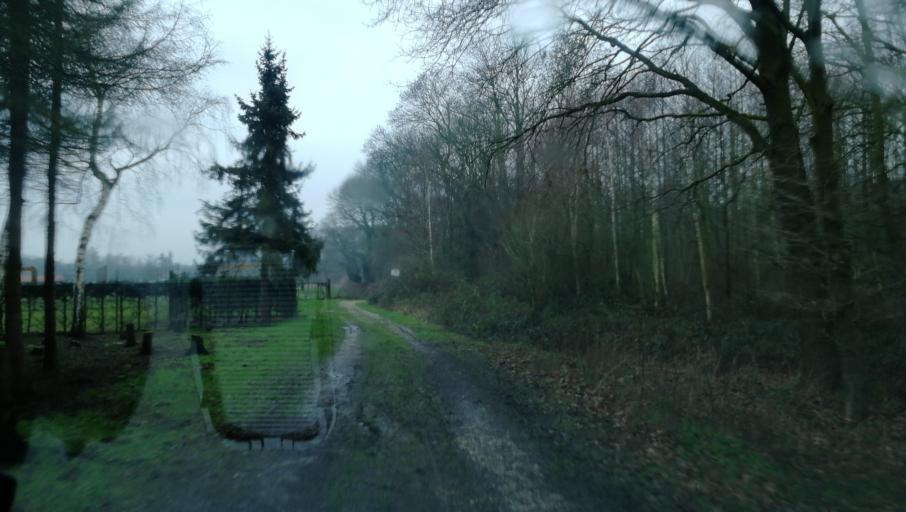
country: NL
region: Limburg
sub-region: Gemeente Venlo
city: Tegelen
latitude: 51.3827
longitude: 6.1177
